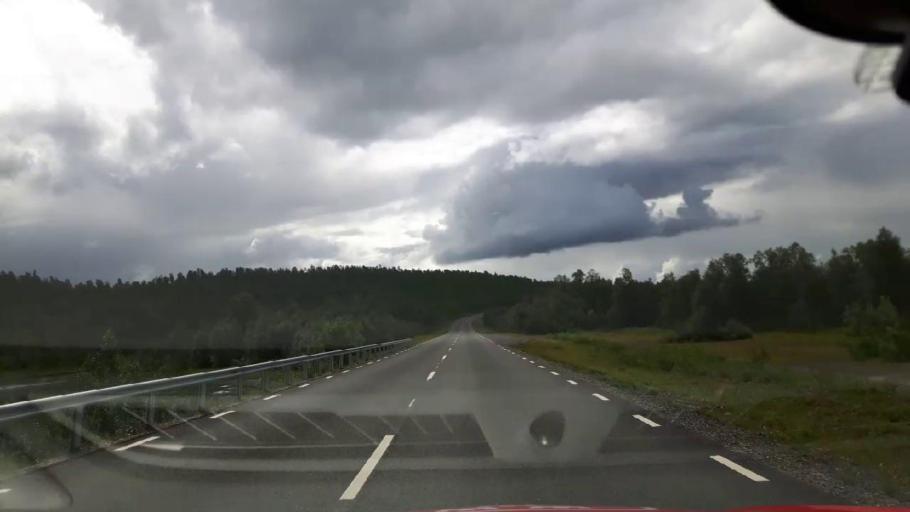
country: NO
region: Nord-Trondelag
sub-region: Royrvik
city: Royrvik
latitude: 64.9774
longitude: 14.2138
